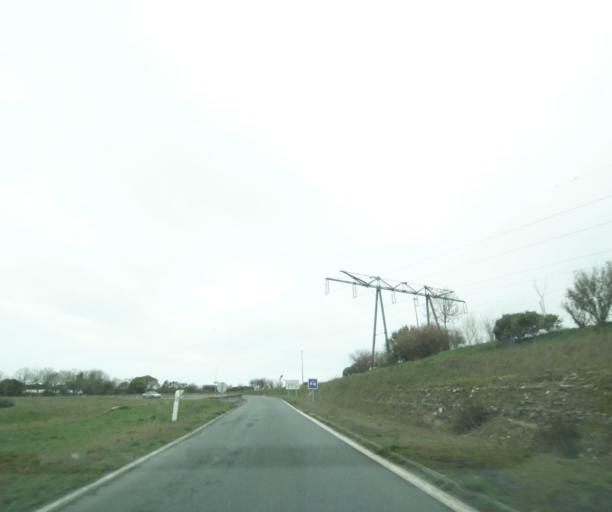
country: FR
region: Poitou-Charentes
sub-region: Departement de la Charente-Maritime
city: Lagord
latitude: 46.1744
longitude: -1.1775
